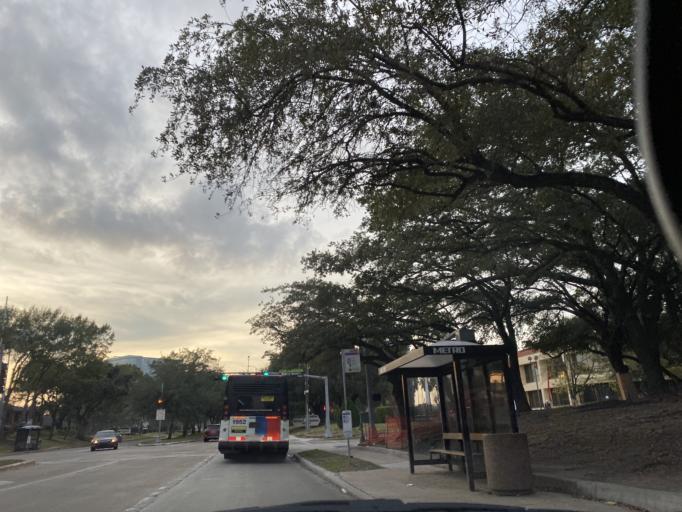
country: US
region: Texas
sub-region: Harris County
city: Bunker Hill Village
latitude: 29.7279
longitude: -95.5675
